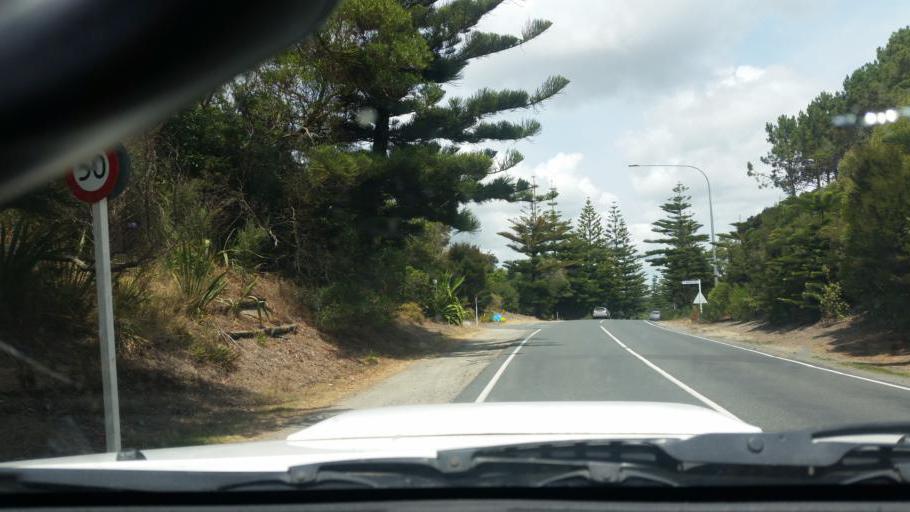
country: NZ
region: Auckland
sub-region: Auckland
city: Wellsford
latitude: -36.1034
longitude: 174.5857
